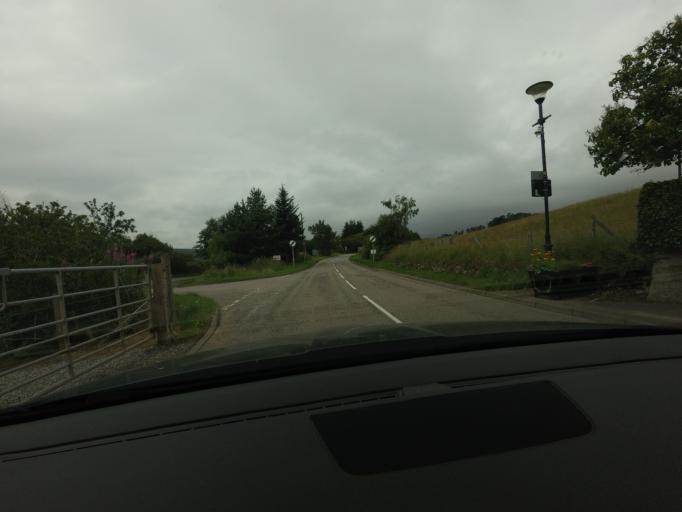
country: GB
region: Scotland
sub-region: Highland
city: Alness
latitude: 58.0284
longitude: -4.4074
